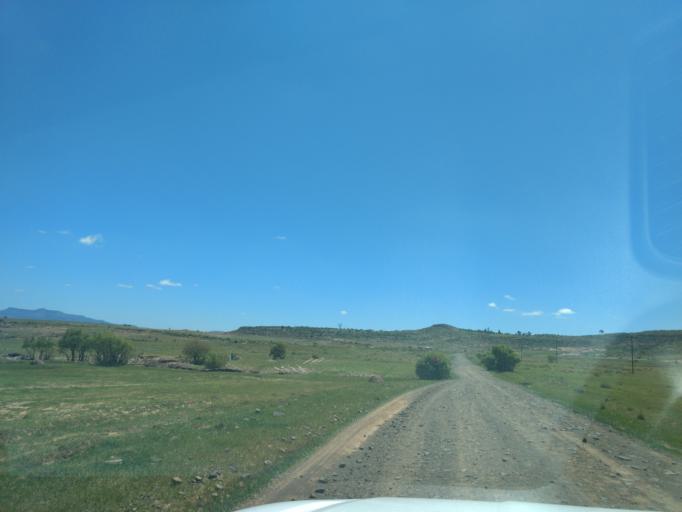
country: LS
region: Maseru
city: Maseru
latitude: -29.4730
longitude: 27.3752
